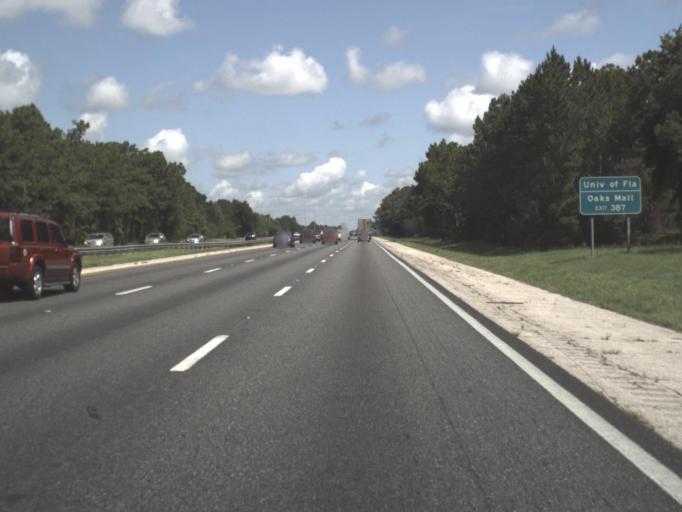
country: US
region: Florida
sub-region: Alachua County
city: Gainesville
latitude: 29.6478
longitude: -82.4087
